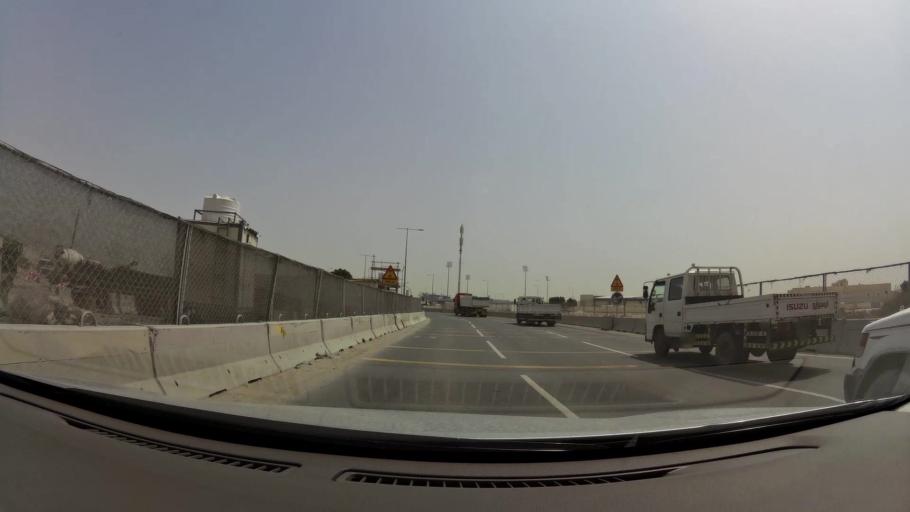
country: QA
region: Al Wakrah
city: Al Wukayr
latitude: 25.1913
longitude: 51.4544
